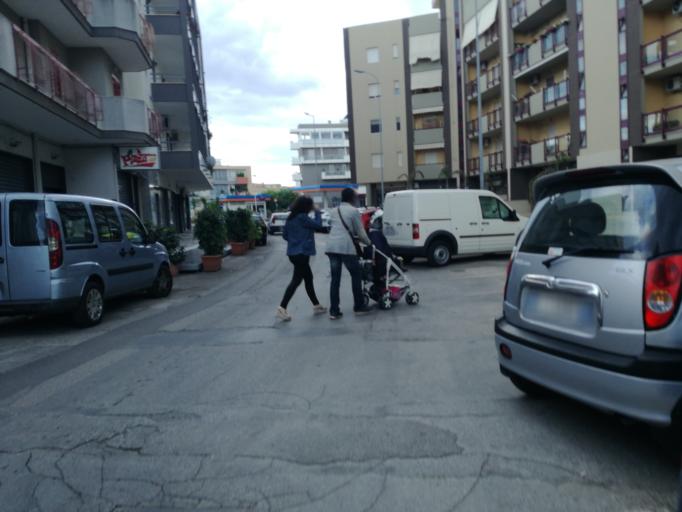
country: IT
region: Apulia
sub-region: Provincia di Bari
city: Triggiano
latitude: 41.0700
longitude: 16.9325
